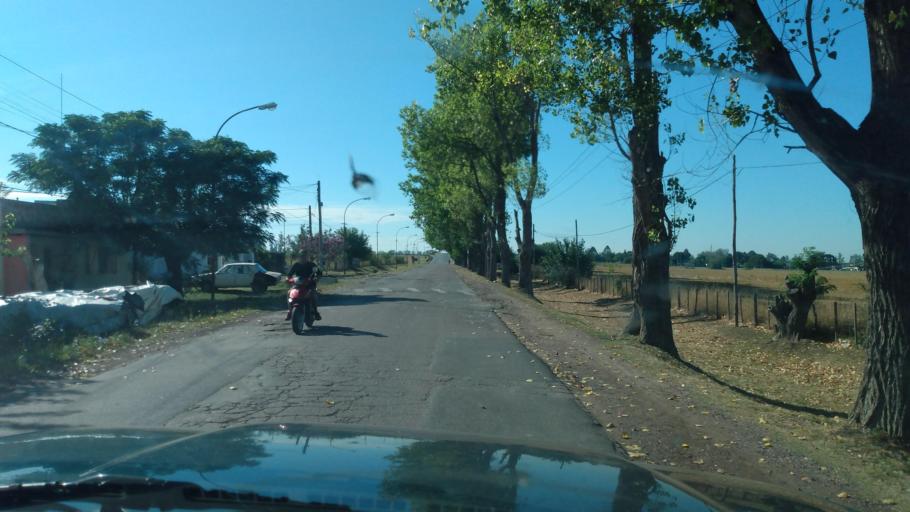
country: AR
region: Buenos Aires
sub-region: Partido de Lujan
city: Lujan
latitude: -34.6037
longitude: -59.1751
